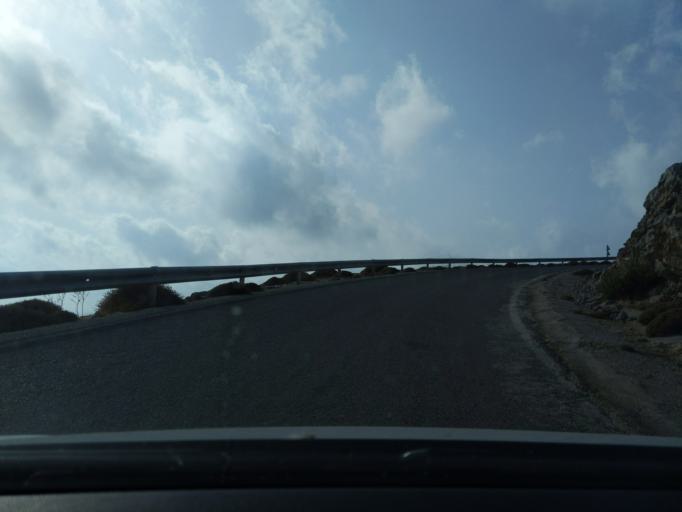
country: GR
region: Crete
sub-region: Nomos Lasithiou
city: Palekastro
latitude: 35.0886
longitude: 26.2674
